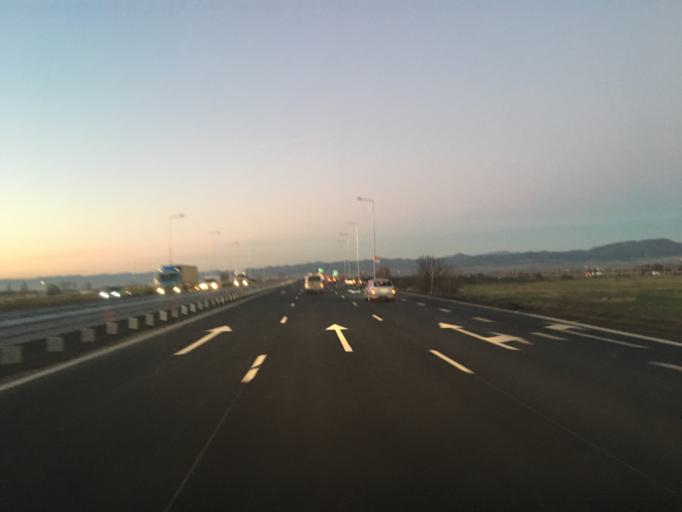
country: BG
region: Sofia-Capital
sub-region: Stolichna Obshtina
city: Sofia
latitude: 42.7029
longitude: 23.4507
